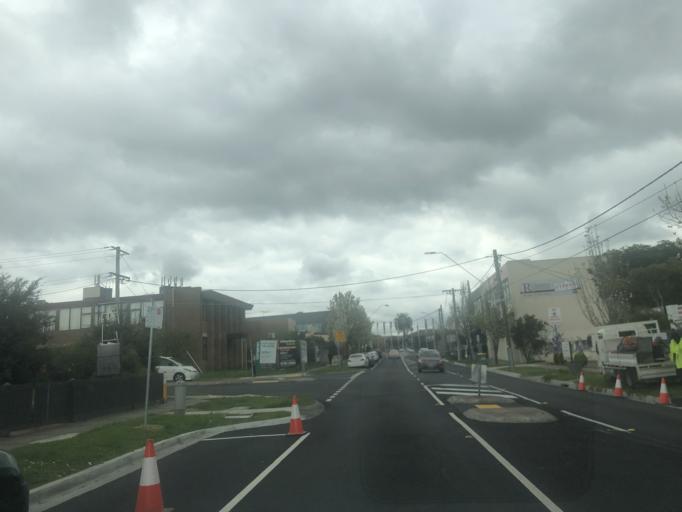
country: AU
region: Victoria
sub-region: Greater Dandenong
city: Dandenong
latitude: -37.9842
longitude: 145.2115
